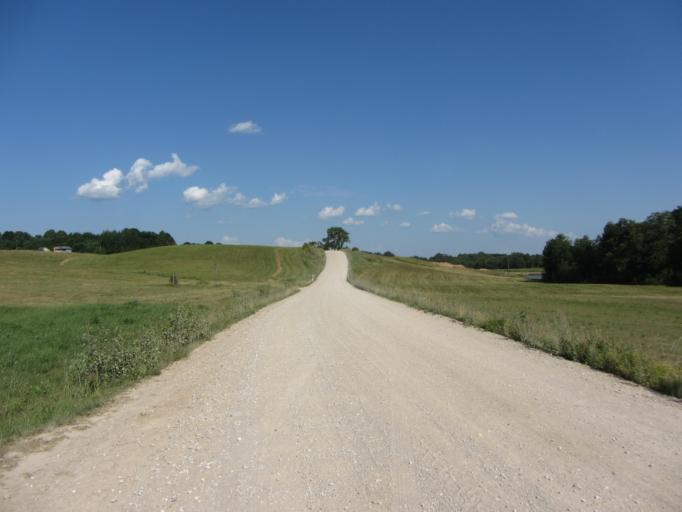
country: LT
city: Moletai
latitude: 55.3511
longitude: 25.2382
